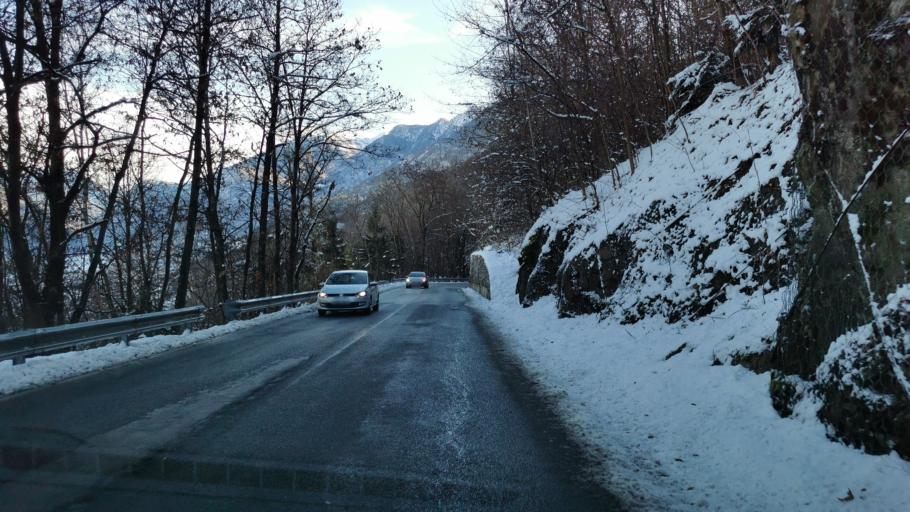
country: IT
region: Lombardy
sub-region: Provincia di Sondrio
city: Regoledo
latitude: 46.1258
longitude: 9.5335
